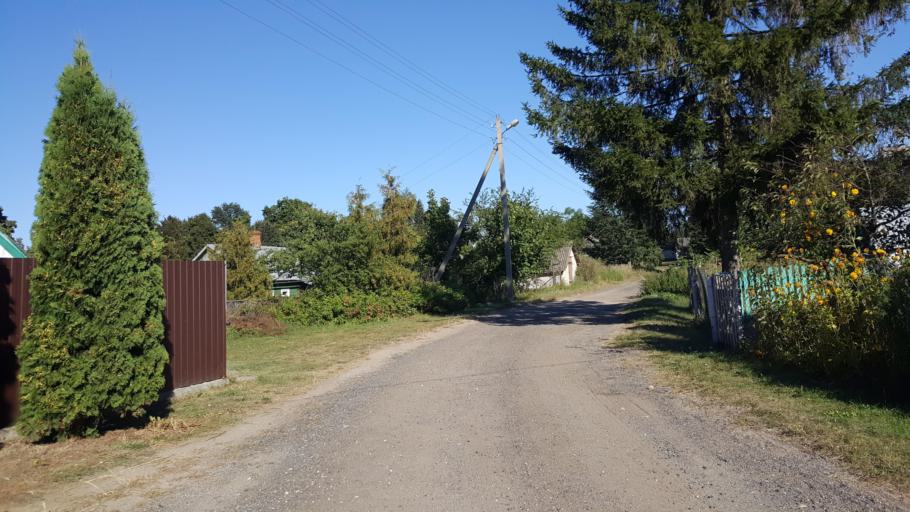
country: PL
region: Lublin Voivodeship
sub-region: Powiat bialski
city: Janow Podlaski
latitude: 52.2627
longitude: 23.2231
